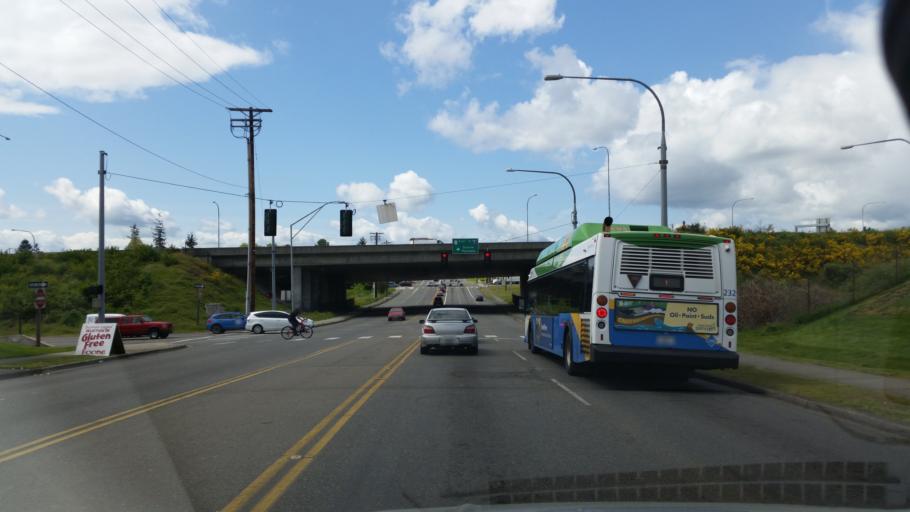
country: US
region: Washington
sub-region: Pierce County
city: Fircrest
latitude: 47.2554
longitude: -122.5123
